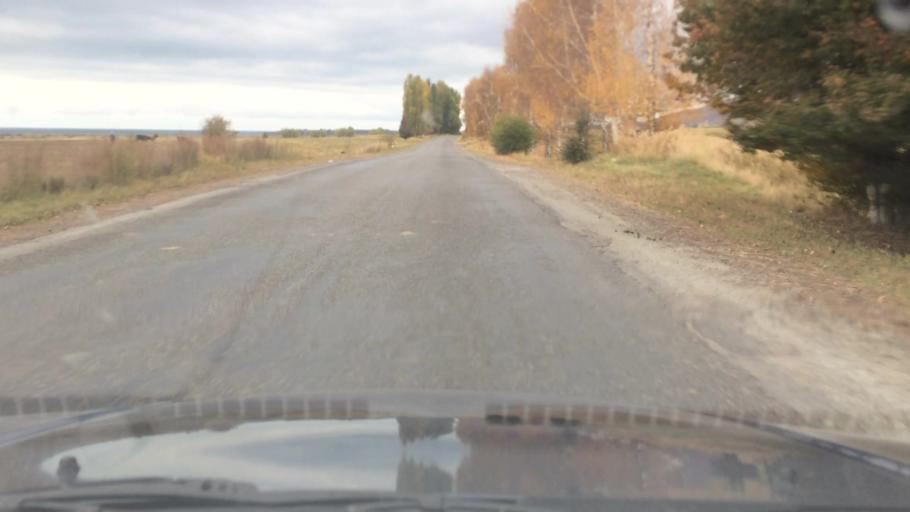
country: KG
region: Ysyk-Koel
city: Tyup
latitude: 42.7646
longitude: 78.1755
